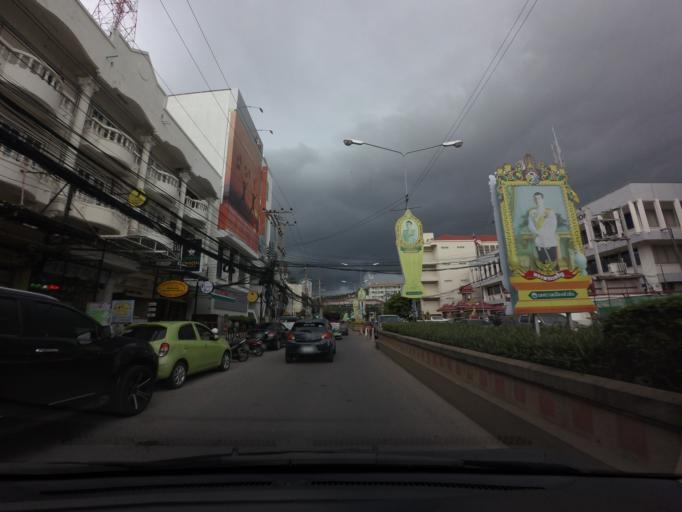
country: TH
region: Prachuap Khiri Khan
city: Hua Hin
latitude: 12.5685
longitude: 99.9586
